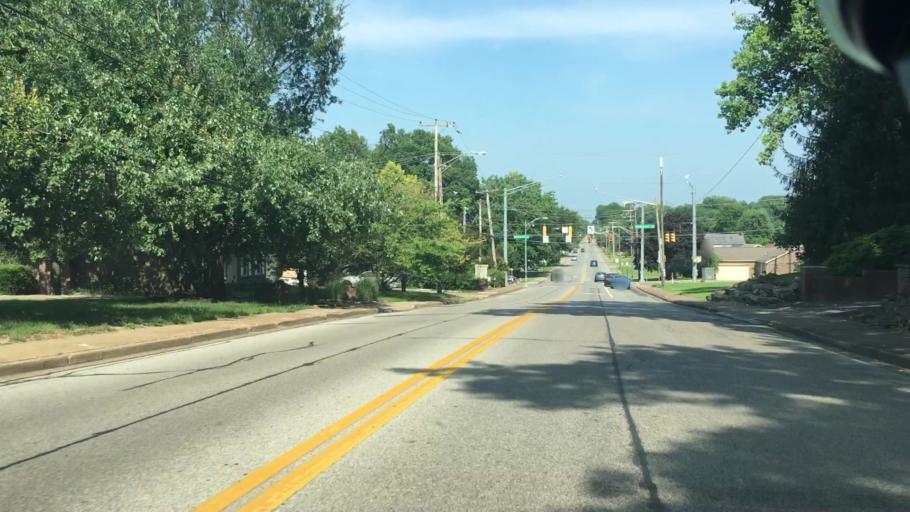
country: US
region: Indiana
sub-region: Vanderburgh County
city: Melody Hill
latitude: 37.9694
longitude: -87.4756
